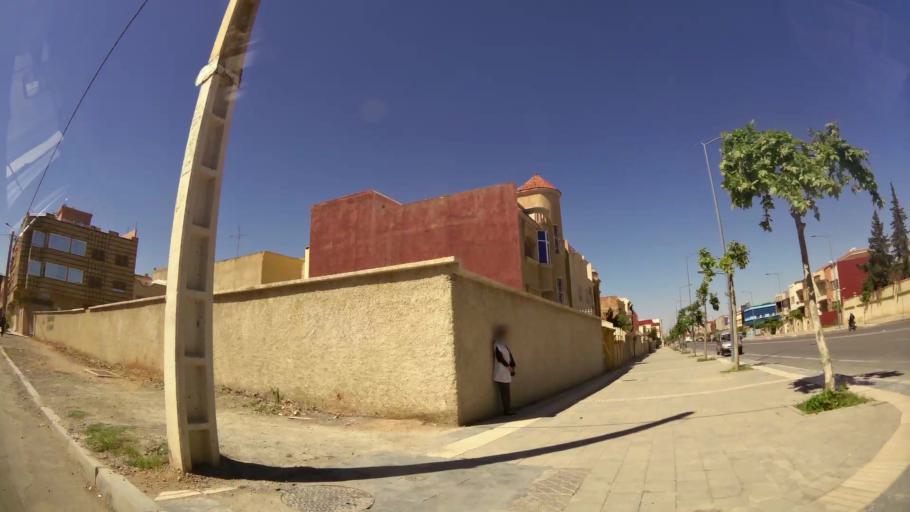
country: MA
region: Oriental
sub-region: Oujda-Angad
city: Oujda
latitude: 34.6670
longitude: -1.8773
